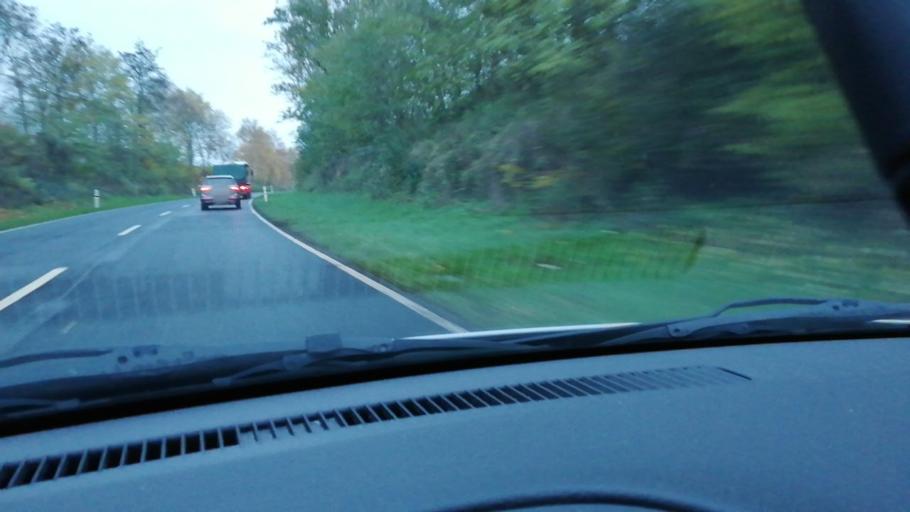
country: DE
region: Bavaria
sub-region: Regierungsbezirk Unterfranken
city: Hosbach
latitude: 50.0254
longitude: 9.2113
